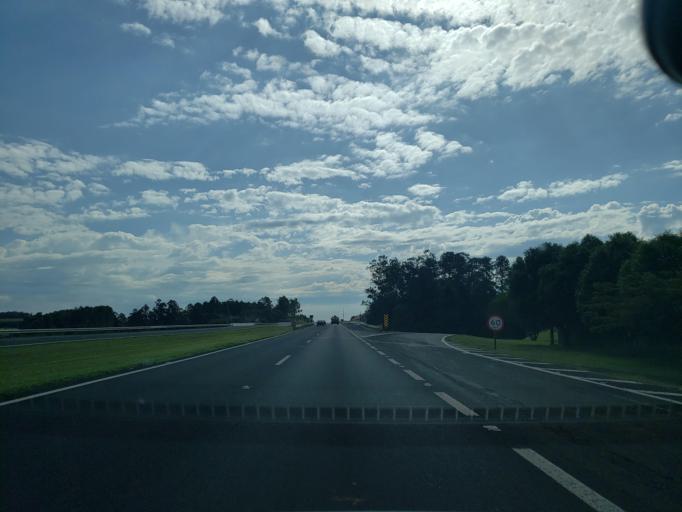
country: BR
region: Sao Paulo
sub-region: Pirajui
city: Pirajui
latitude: -21.9844
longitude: -49.4450
